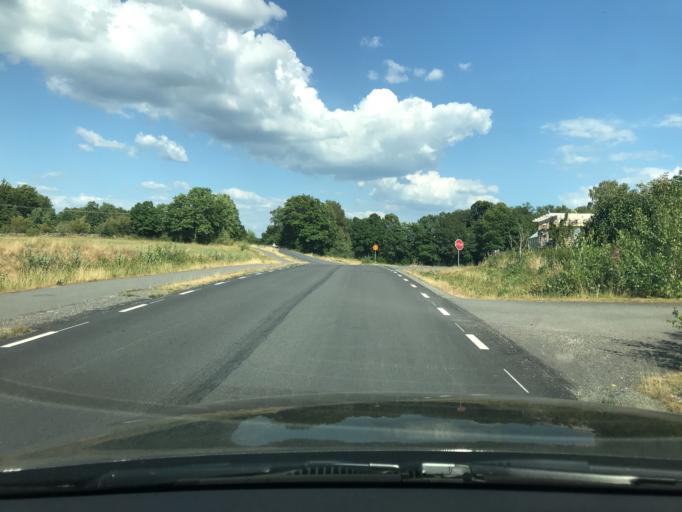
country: SE
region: Skane
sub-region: Hassleholms Kommun
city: Hastveda
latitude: 56.2730
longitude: 13.9044
